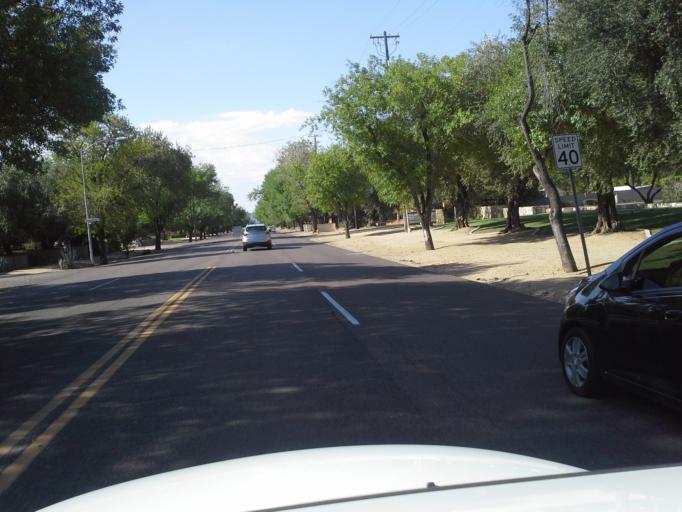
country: US
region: Arizona
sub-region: Maricopa County
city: Phoenix
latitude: 33.5301
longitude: -112.0738
